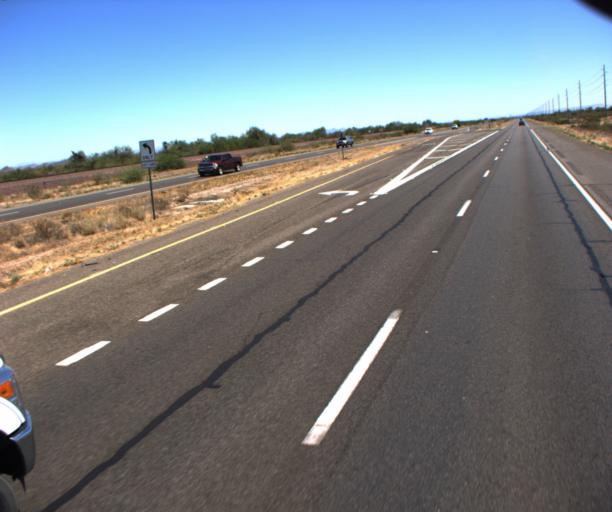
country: US
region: Arizona
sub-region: Maricopa County
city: Sun City West
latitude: 33.7347
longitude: -112.4735
